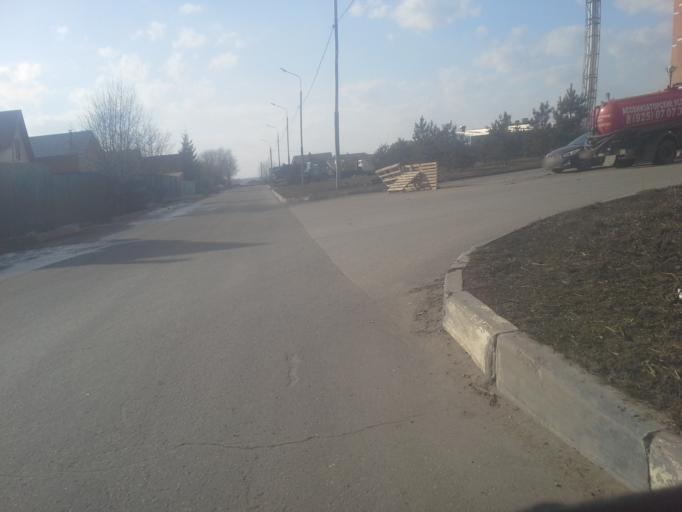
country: RU
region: Moskovskaya
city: Shcherbinka
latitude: 55.4659
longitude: 37.5423
